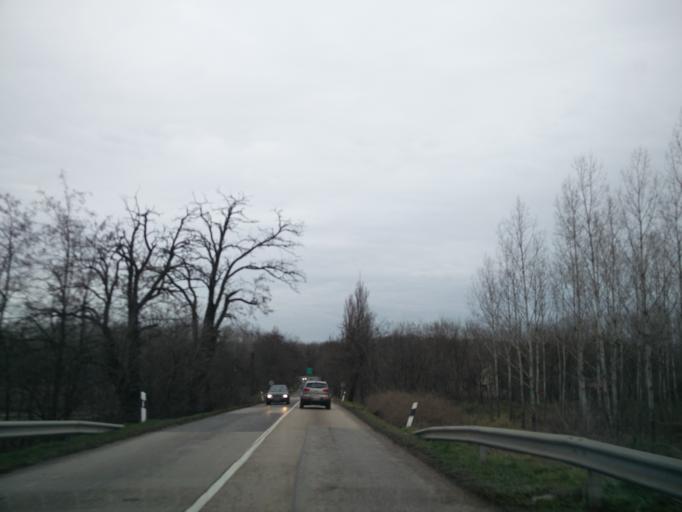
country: HU
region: Pest
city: Gyomro
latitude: 47.4272
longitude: 19.4197
